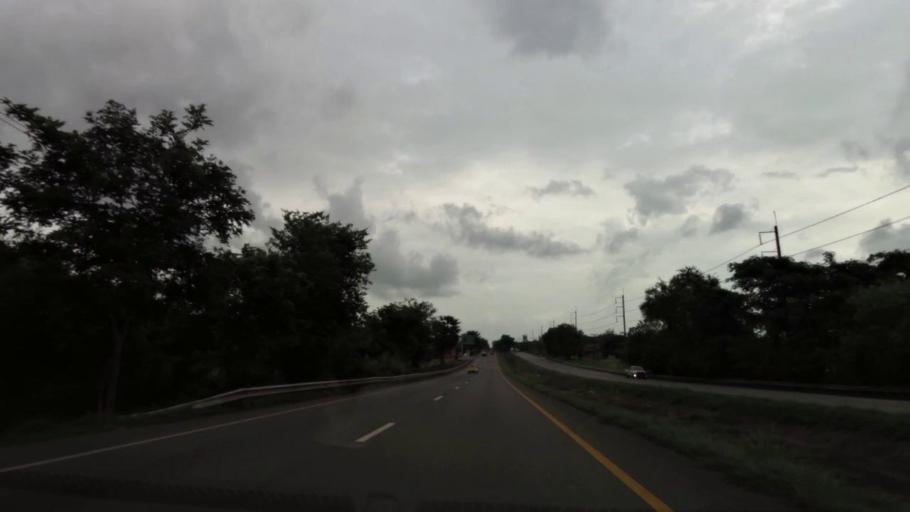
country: TH
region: Chanthaburi
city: Tha Mai
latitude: 12.7062
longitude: 101.9837
